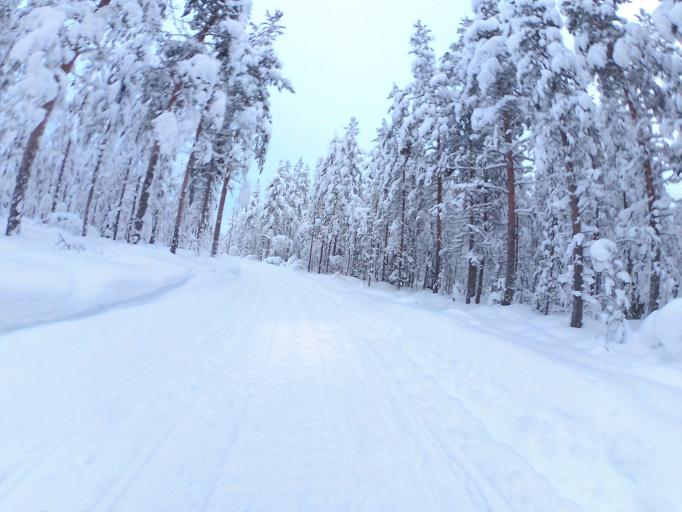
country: FI
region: Lapland
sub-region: Rovaniemi
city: Rovaniemi
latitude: 66.6279
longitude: 26.0379
